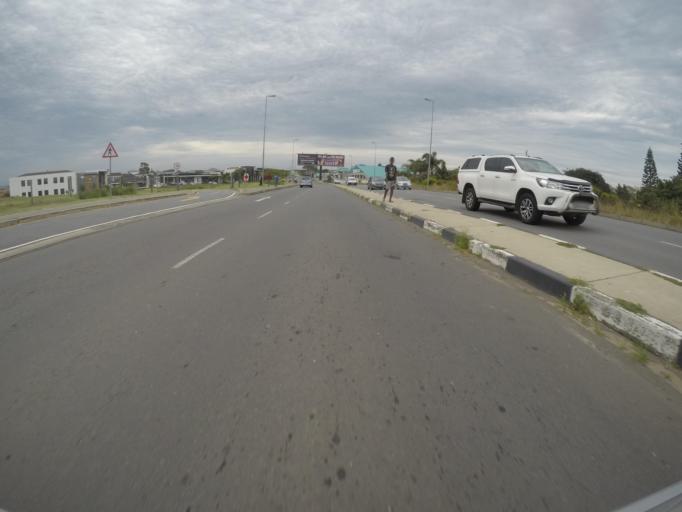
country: ZA
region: Eastern Cape
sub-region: Buffalo City Metropolitan Municipality
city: East London
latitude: -32.9594
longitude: 27.9351
